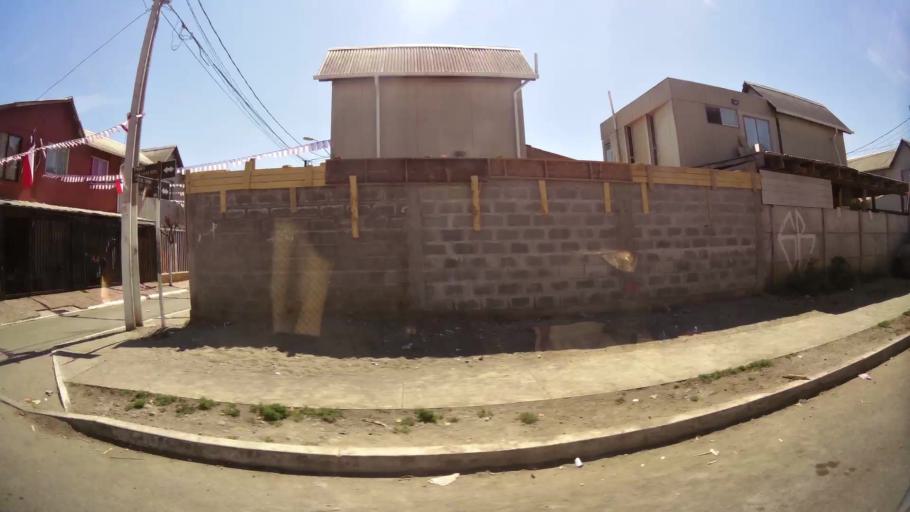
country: CL
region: Santiago Metropolitan
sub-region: Provincia de Talagante
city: Penaflor
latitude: -33.6147
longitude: -70.9026
